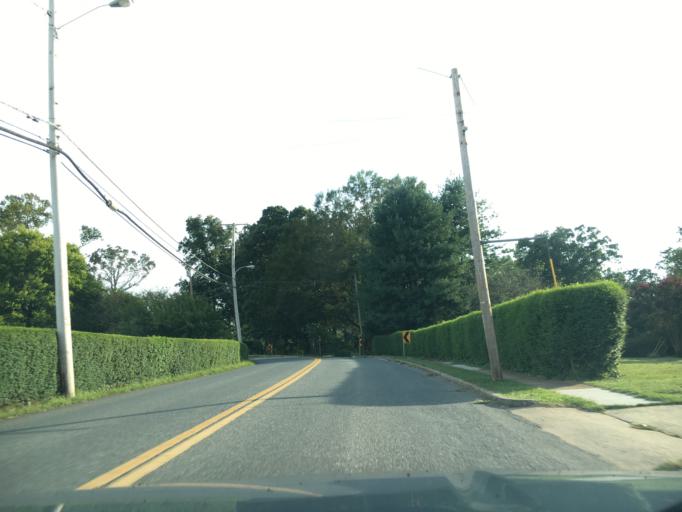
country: US
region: Virginia
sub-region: City of Lynchburg
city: West Lynchburg
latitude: 37.4372
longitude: -79.1962
